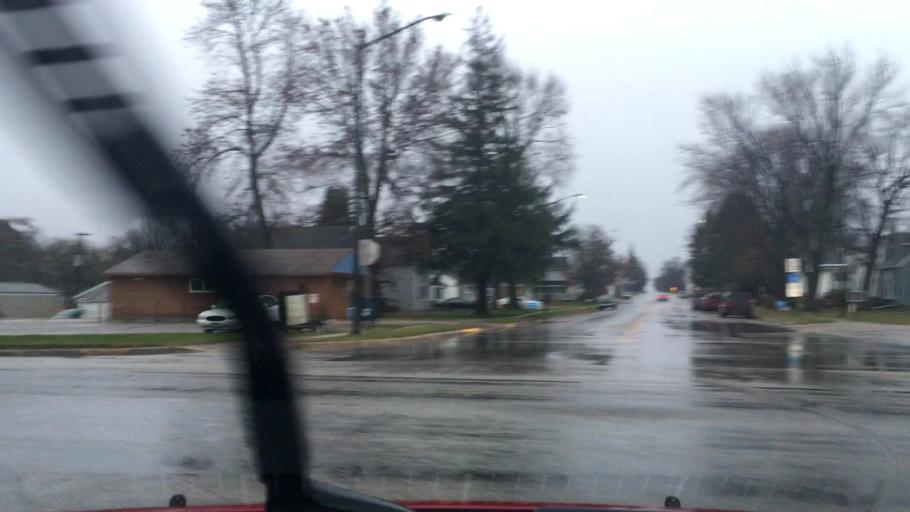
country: US
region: Minnesota
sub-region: Fillmore County
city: Harmony
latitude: 43.5331
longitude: -91.9294
